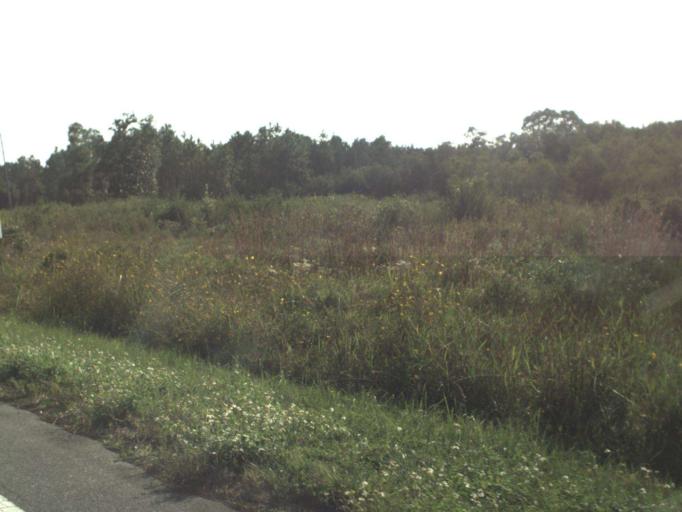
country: US
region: Florida
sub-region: Franklin County
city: Carrabelle
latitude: 29.9429
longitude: -84.5008
